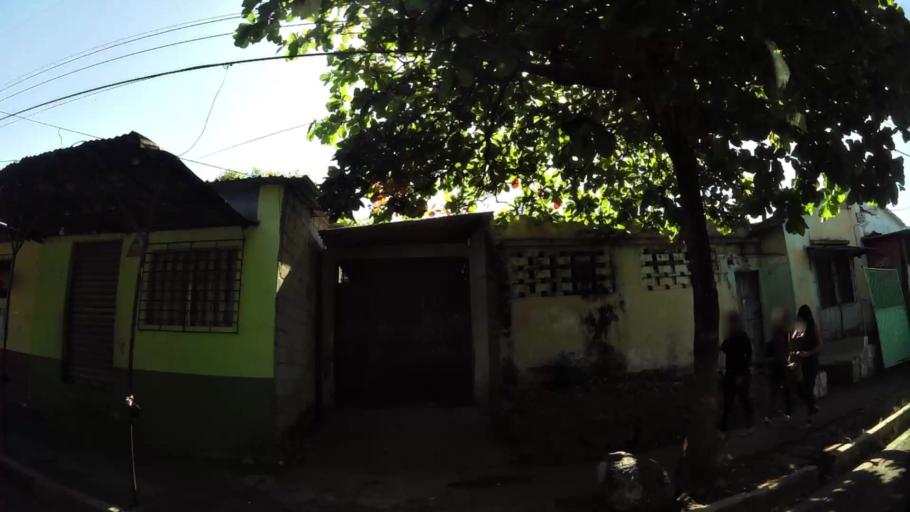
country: SV
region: Sonsonate
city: Sonzacate
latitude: 13.7298
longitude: -89.7195
